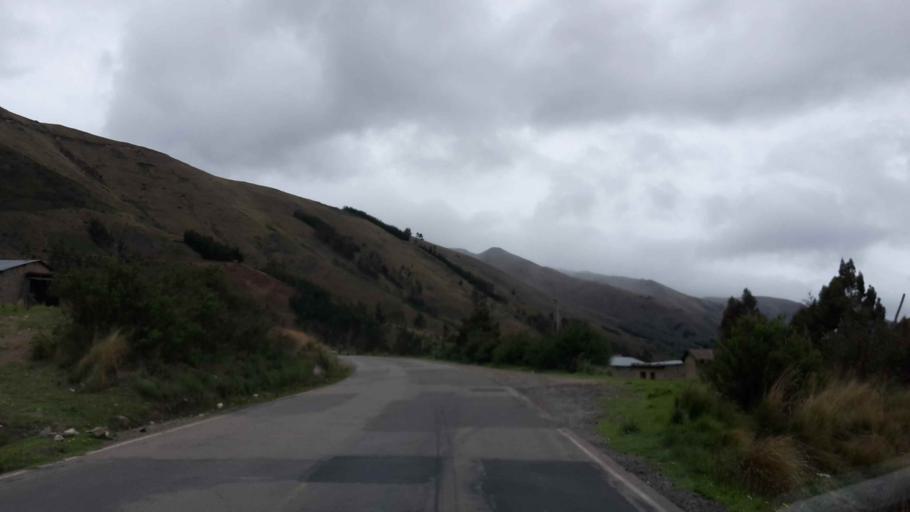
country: BO
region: Cochabamba
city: Arani
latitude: -17.4833
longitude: -65.5473
